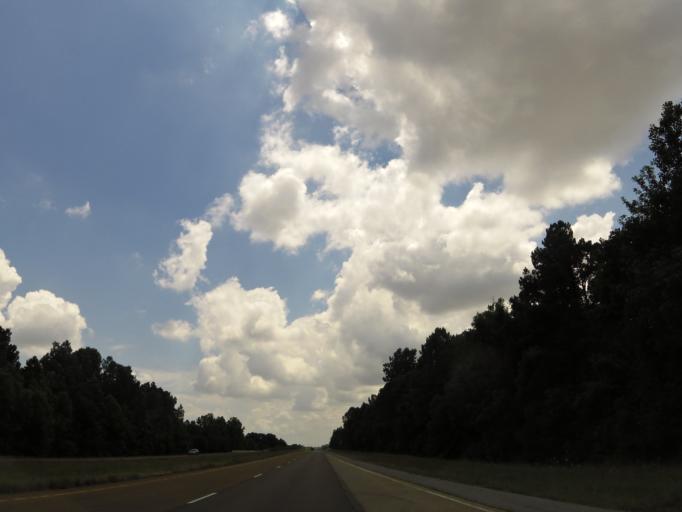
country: US
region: Tennessee
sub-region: Dyer County
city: Dyersburg
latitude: 36.0199
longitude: -89.3409
